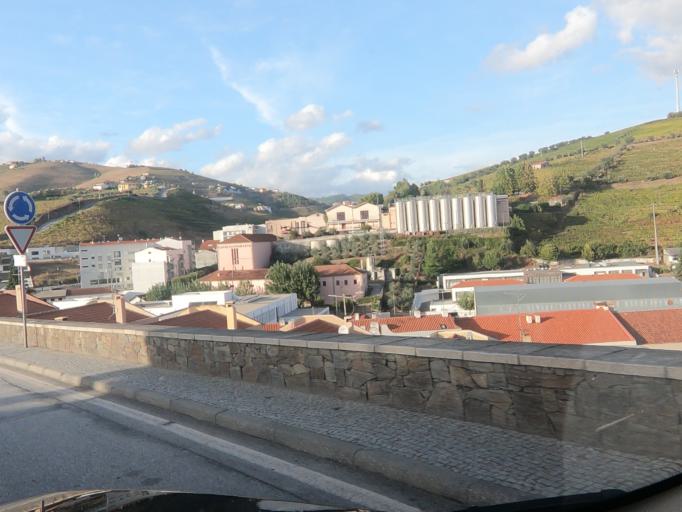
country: PT
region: Vila Real
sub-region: Santa Marta de Penaguiao
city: Santa Marta de Penaguiao
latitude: 41.2088
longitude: -7.7845
